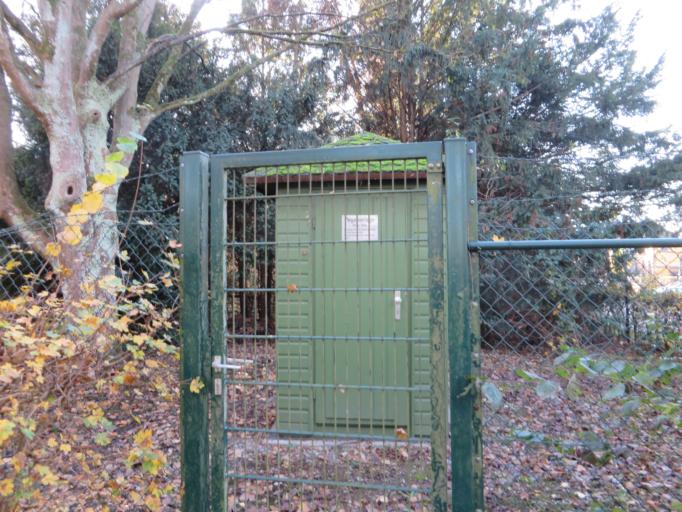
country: DE
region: North Rhine-Westphalia
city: Witten
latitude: 51.4250
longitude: 7.3012
